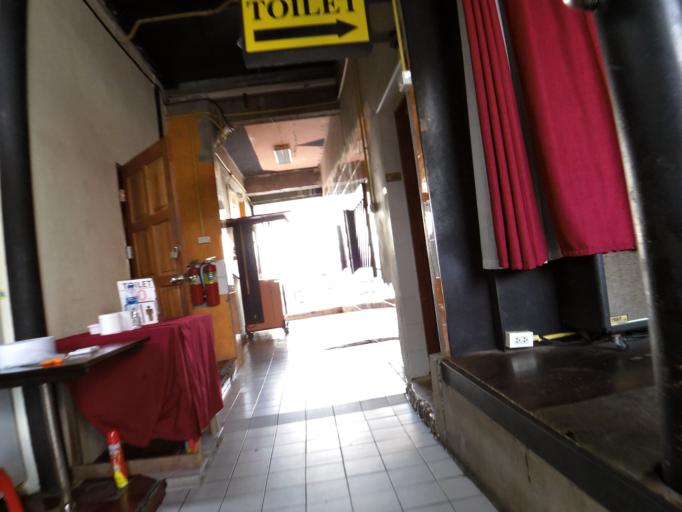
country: TH
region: Phuket
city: Patong
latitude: 7.8942
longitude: 98.2967
